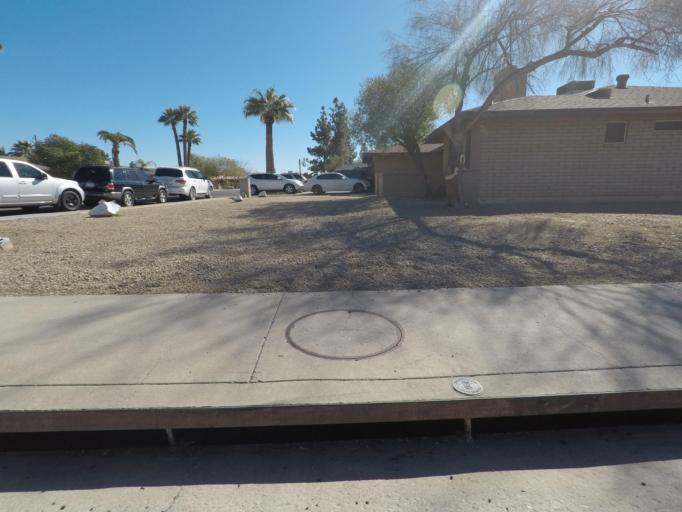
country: US
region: Arizona
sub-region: Maricopa County
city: Glendale
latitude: 33.5401
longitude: -112.1219
